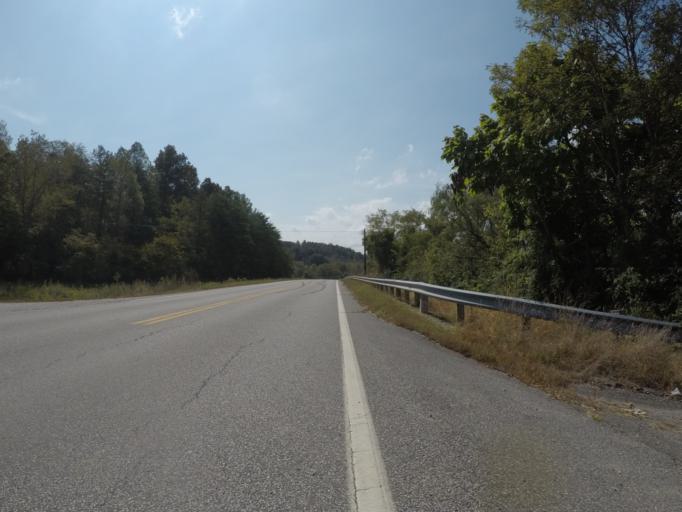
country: US
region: West Virginia
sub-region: Cabell County
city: Lesage
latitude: 38.5118
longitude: -82.3923
